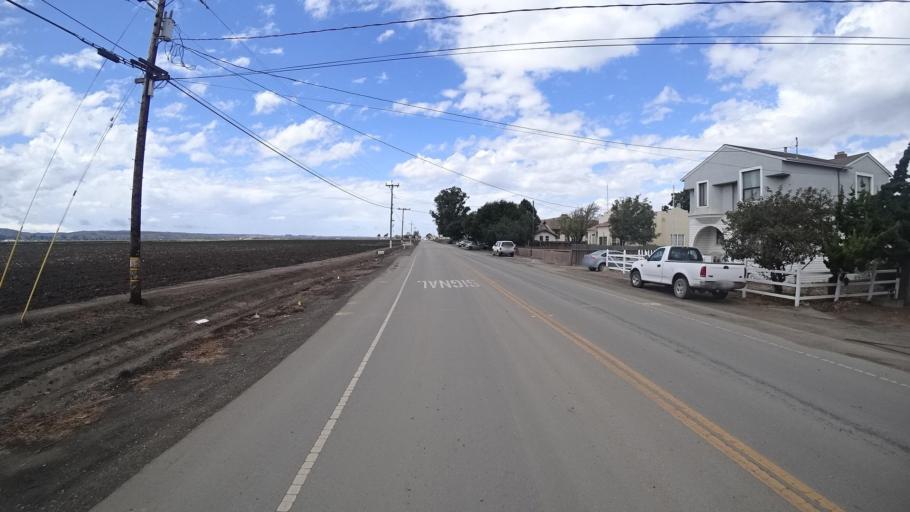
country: US
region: California
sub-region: Monterey County
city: Salinas
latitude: 36.6452
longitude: -121.6669
